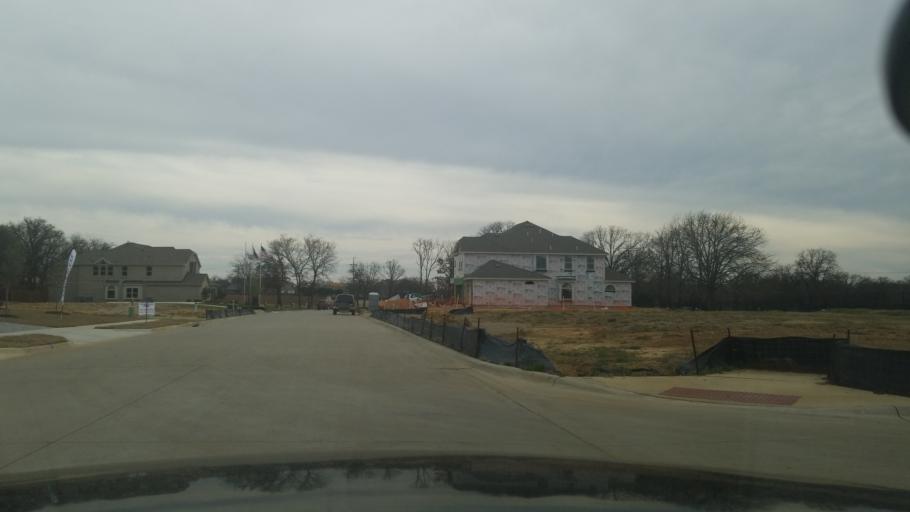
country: US
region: Texas
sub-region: Denton County
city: Corinth
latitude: 33.1328
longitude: -97.0770
